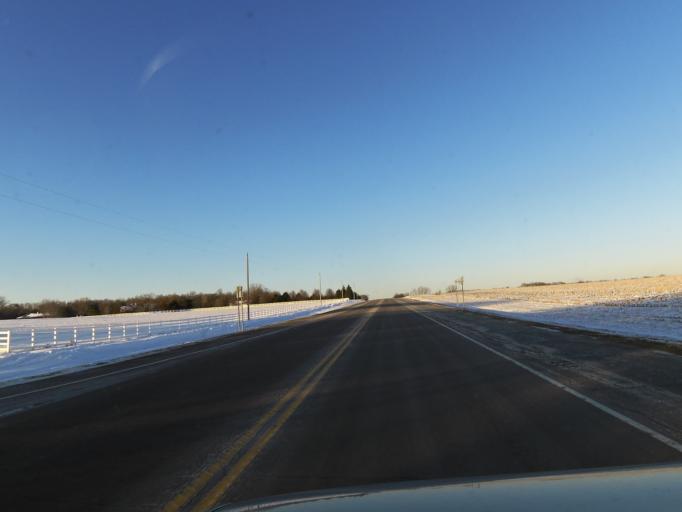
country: US
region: Minnesota
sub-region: Dakota County
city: Farmington
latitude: 44.5807
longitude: -93.1368
